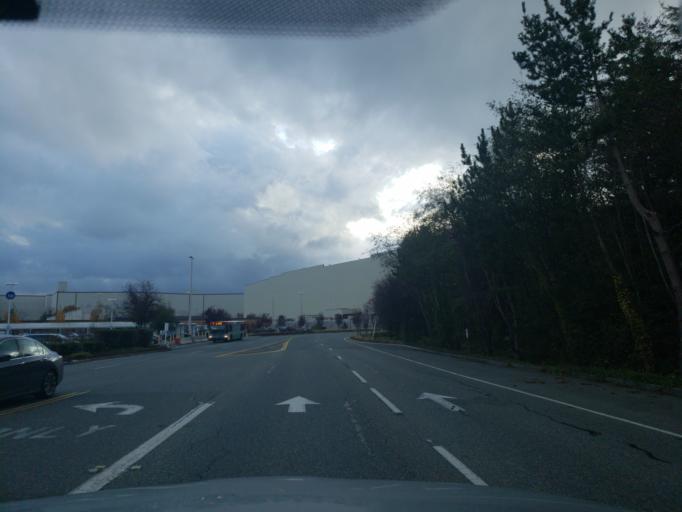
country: US
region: Washington
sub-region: Snohomish County
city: Mukilteo
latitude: 47.9320
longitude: -122.2657
